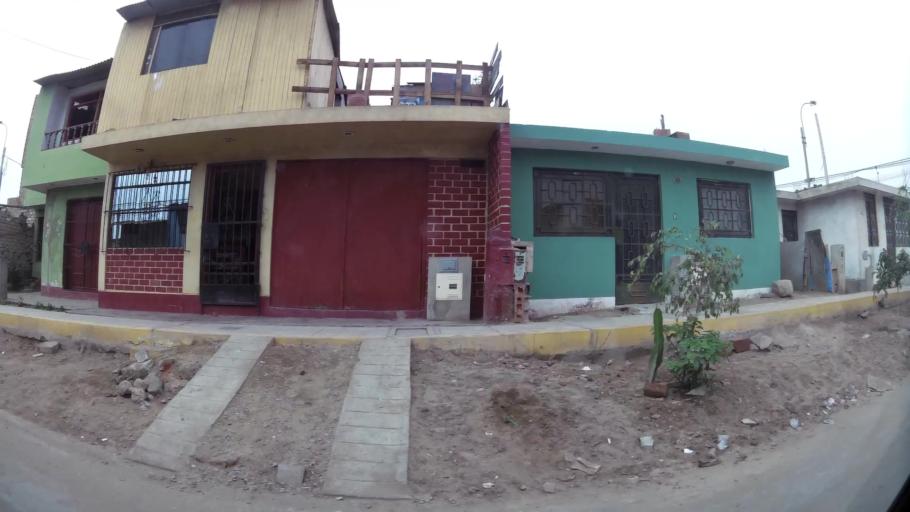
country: PE
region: Lima
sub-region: Lima
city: Surco
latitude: -12.2225
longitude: -76.9449
